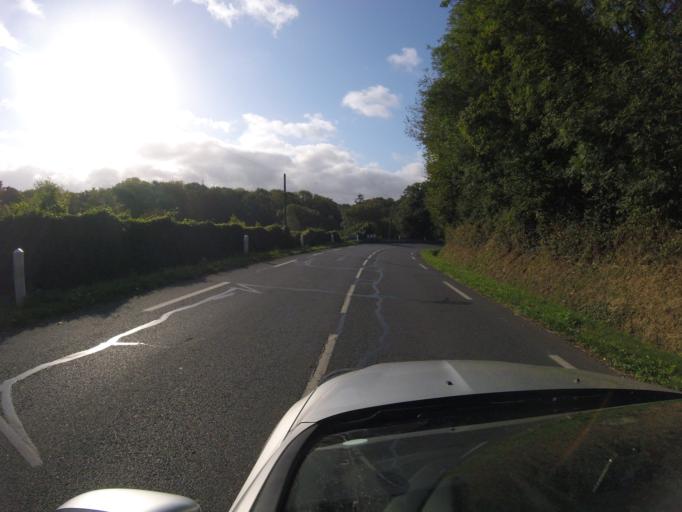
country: FR
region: Haute-Normandie
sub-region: Departement de la Seine-Maritime
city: Fecamp
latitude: 49.7652
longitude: 0.4049
